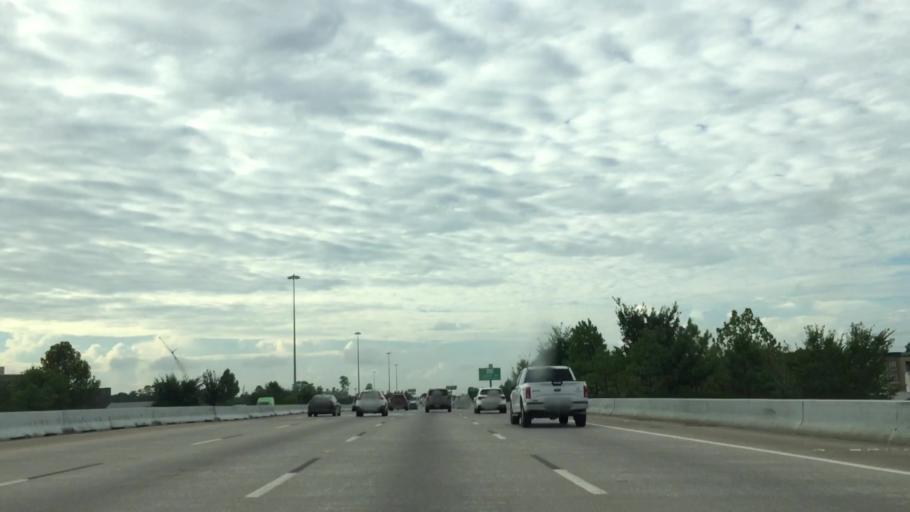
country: US
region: Texas
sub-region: Harris County
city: Oak Cliff Place
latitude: 29.9809
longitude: -95.5676
